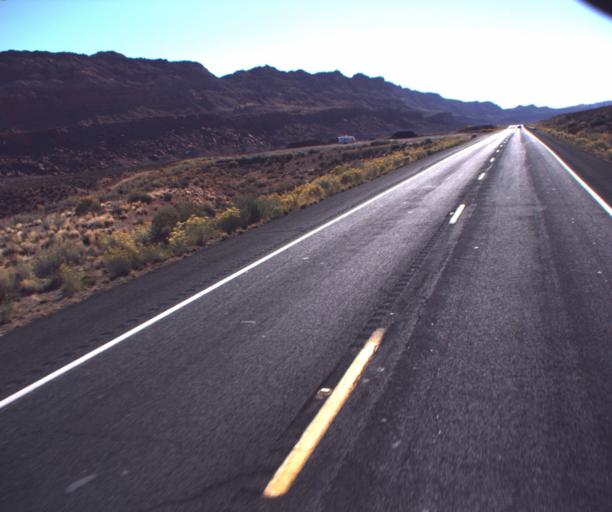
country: US
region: Arizona
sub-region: Coconino County
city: Tuba City
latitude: 36.2619
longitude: -111.4267
